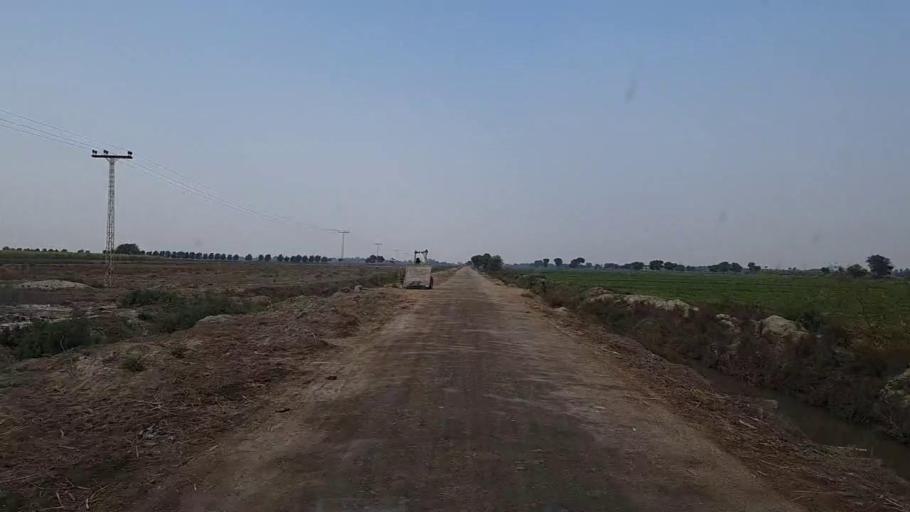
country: PK
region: Sindh
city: Mirwah Gorchani
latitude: 25.3759
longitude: 69.0718
